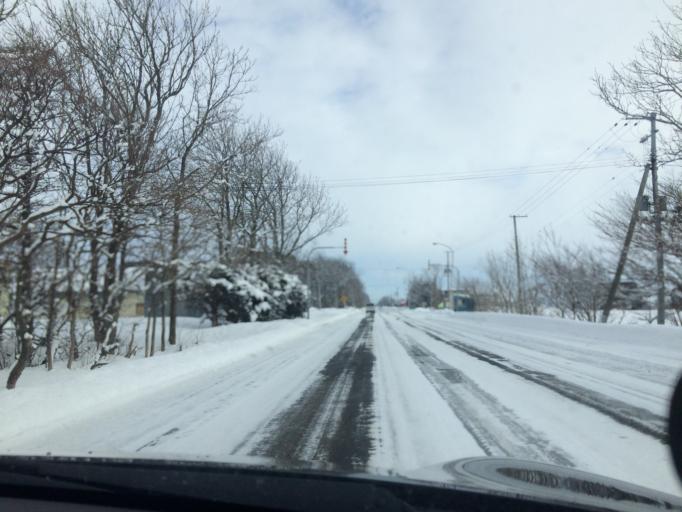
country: JP
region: Hokkaido
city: Kitahiroshima
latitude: 43.0332
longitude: 141.6061
